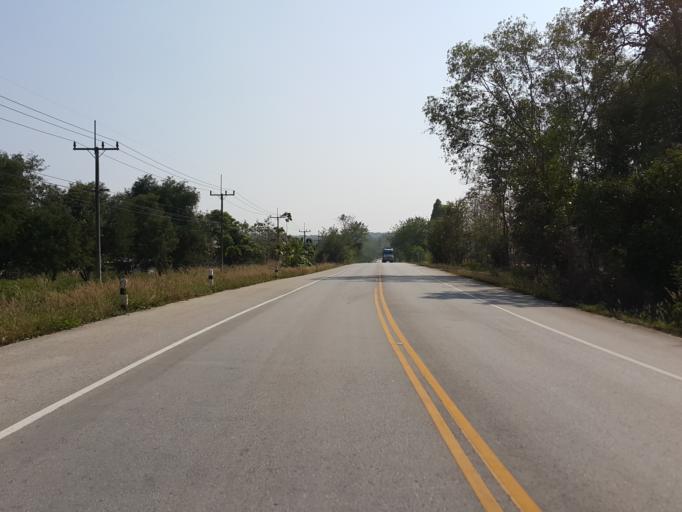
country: TH
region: Lampang
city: Wang Nuea
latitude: 18.9673
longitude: 99.6121
